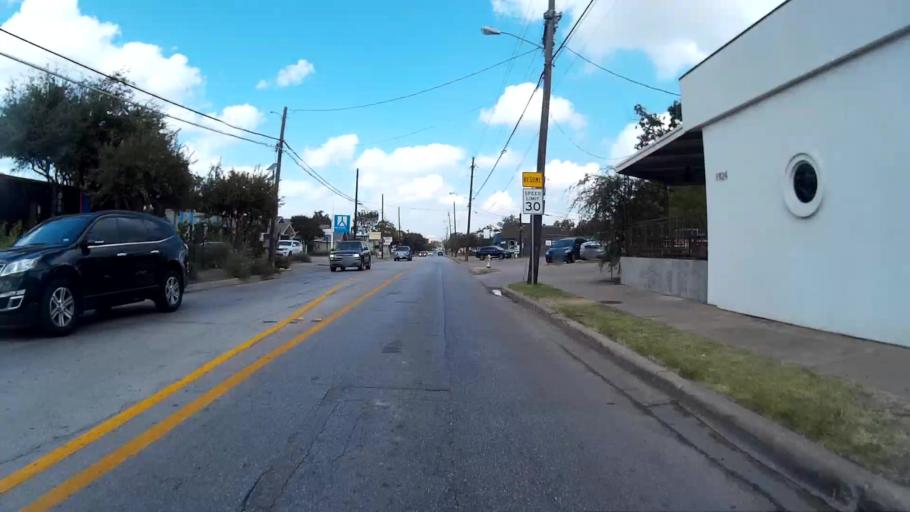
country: US
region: Texas
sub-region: Dallas County
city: Highland Park
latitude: 32.8118
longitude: -96.7750
